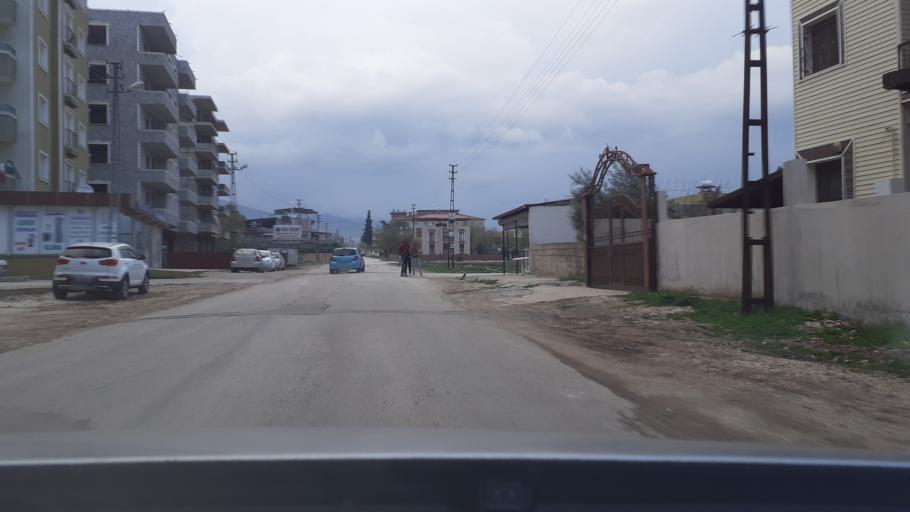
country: TR
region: Hatay
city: Kirikhan
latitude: 36.4843
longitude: 36.3555
